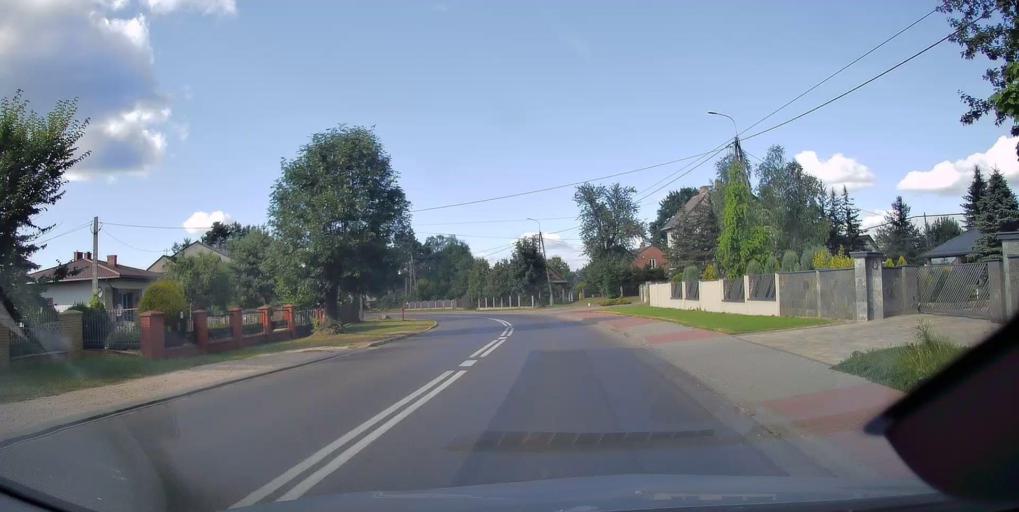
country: PL
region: Swietokrzyskie
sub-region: Powiat skarzyski
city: Suchedniow
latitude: 51.0312
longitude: 20.8396
